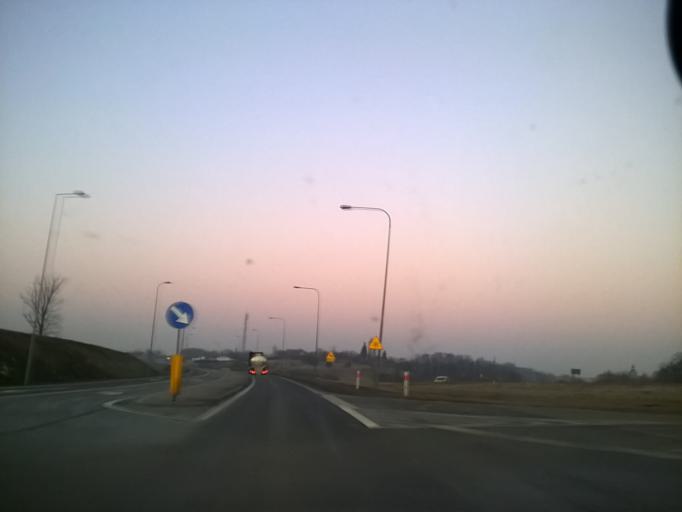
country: PL
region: Warmian-Masurian Voivodeship
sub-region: Powiat olsztynski
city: Barczewo
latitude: 53.8266
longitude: 20.6726
